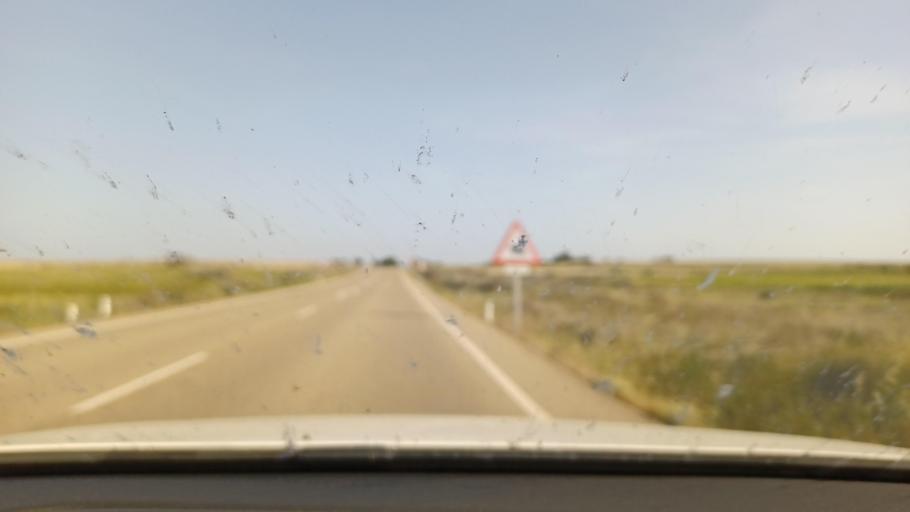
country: ES
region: Aragon
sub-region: Provincia de Zaragoza
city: Chiprana
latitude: 41.3678
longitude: -0.1091
